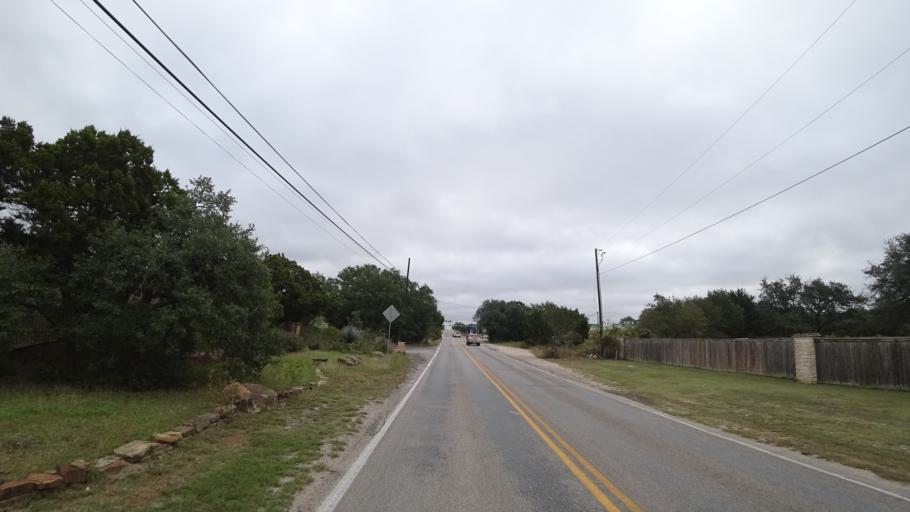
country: US
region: Texas
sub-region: Travis County
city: Barton Creek
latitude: 30.2600
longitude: -97.9091
